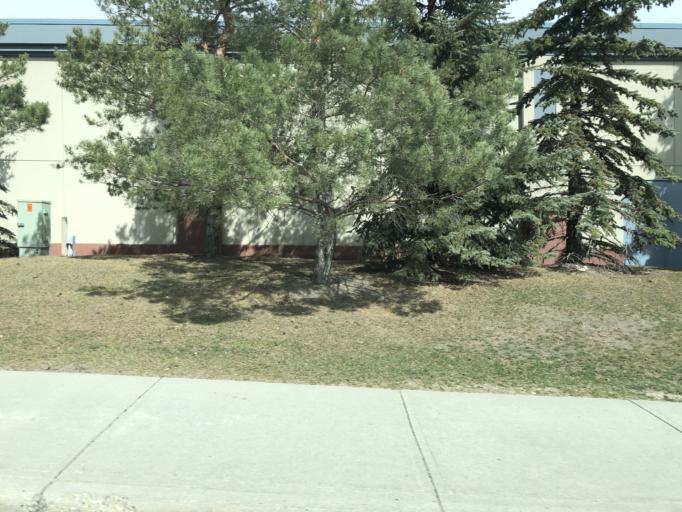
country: CA
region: Alberta
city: Calgary
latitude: 51.0728
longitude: -113.9905
